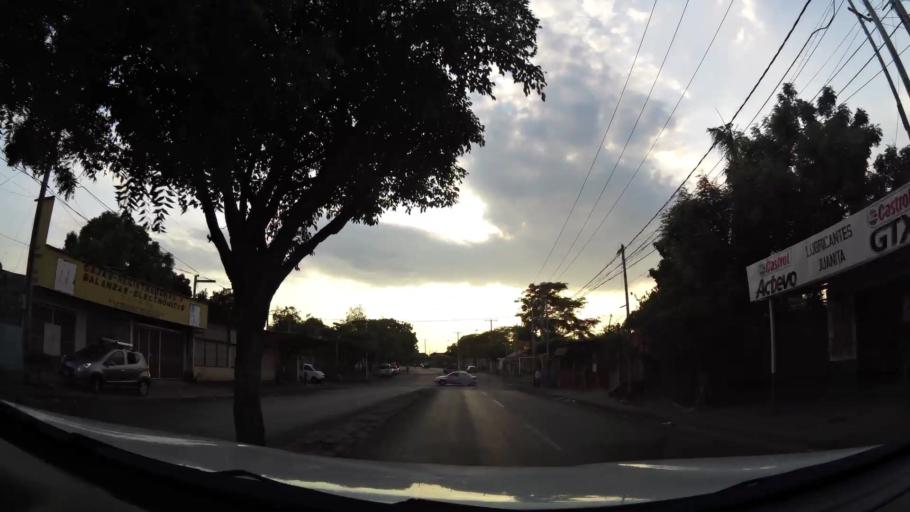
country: NI
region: Managua
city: Managua
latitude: 12.1464
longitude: -86.2462
